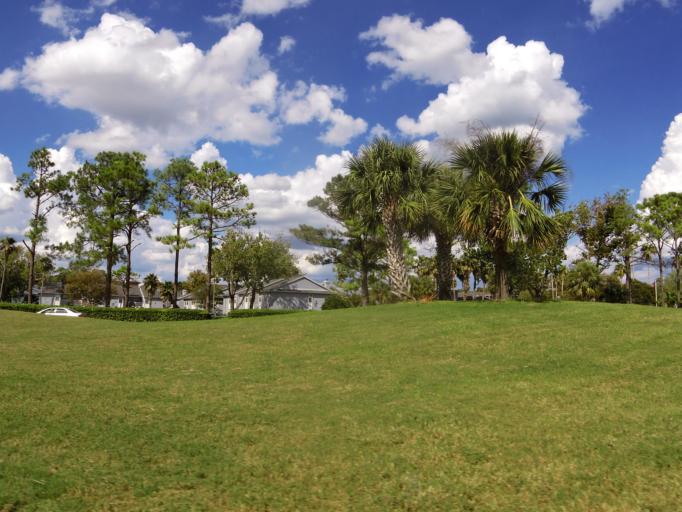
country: US
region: Florida
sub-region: Saint Johns County
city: Ponte Vedra Beach
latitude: 30.2505
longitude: -81.3969
